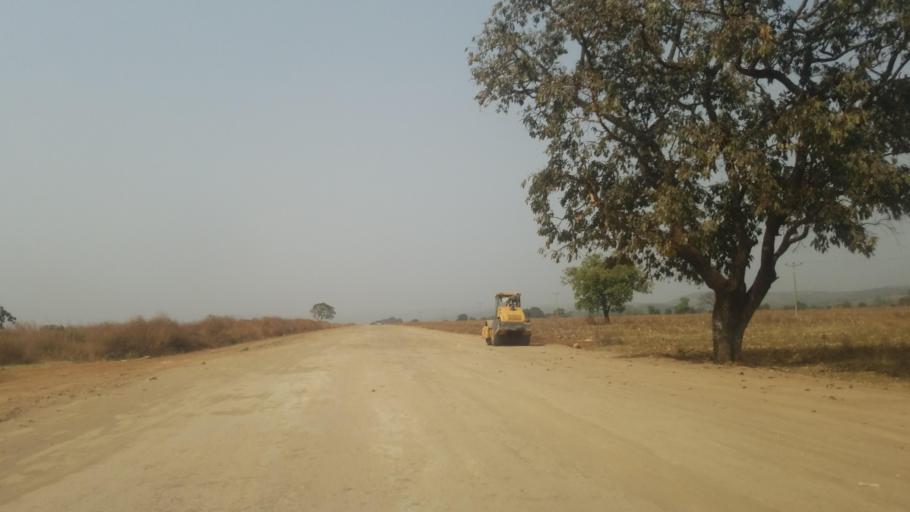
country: ET
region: Amhara
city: Bure
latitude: 10.8959
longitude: 36.4601
